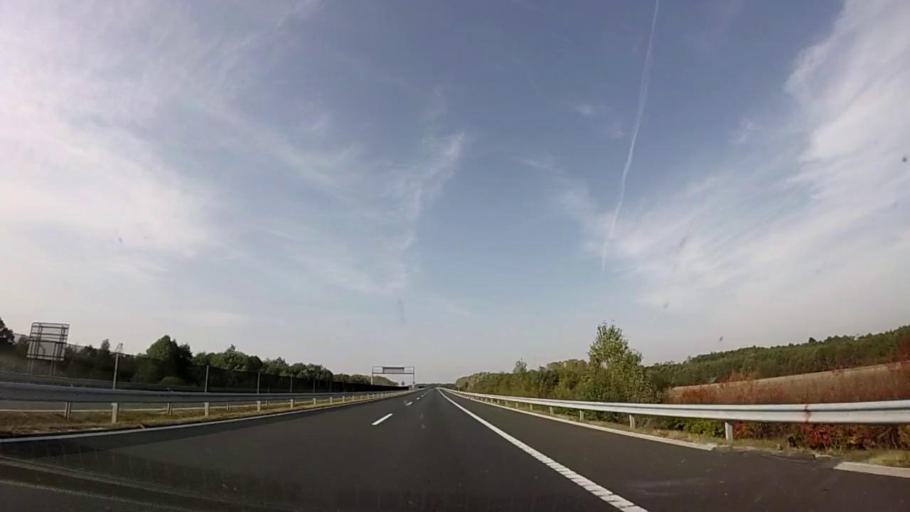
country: HU
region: Zala
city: Zalakomar
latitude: 46.5064
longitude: 17.1687
